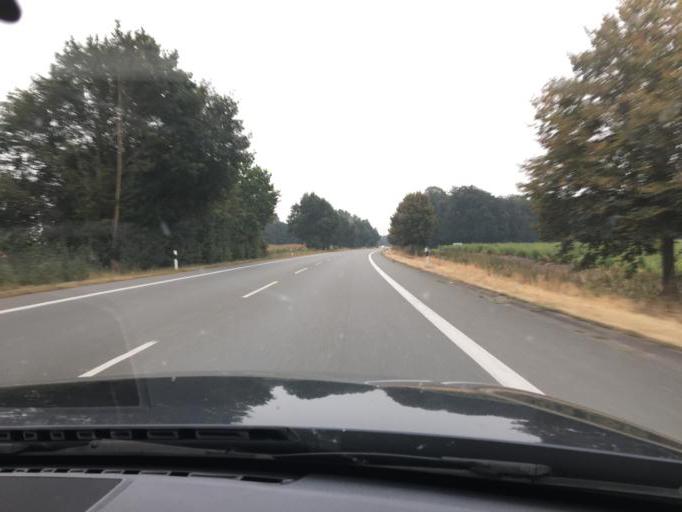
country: DE
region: North Rhine-Westphalia
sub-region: Regierungsbezirk Munster
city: Greven
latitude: 52.0651
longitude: 7.6692
